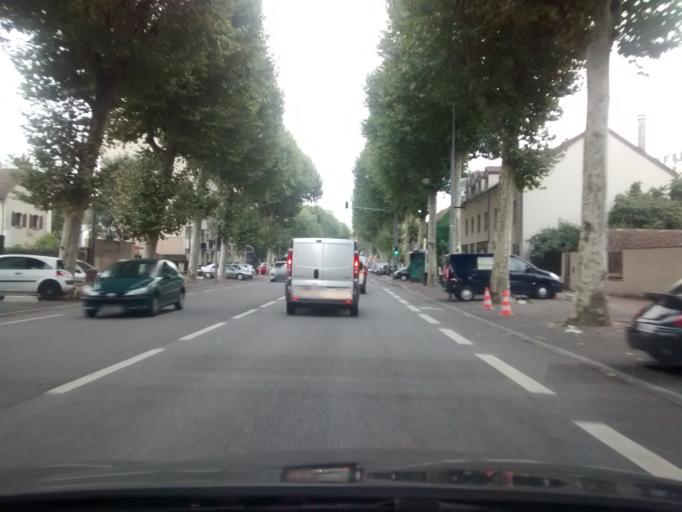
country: FR
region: Ile-de-France
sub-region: Departement des Yvelines
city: Viroflay
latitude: 48.8025
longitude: 2.1651
